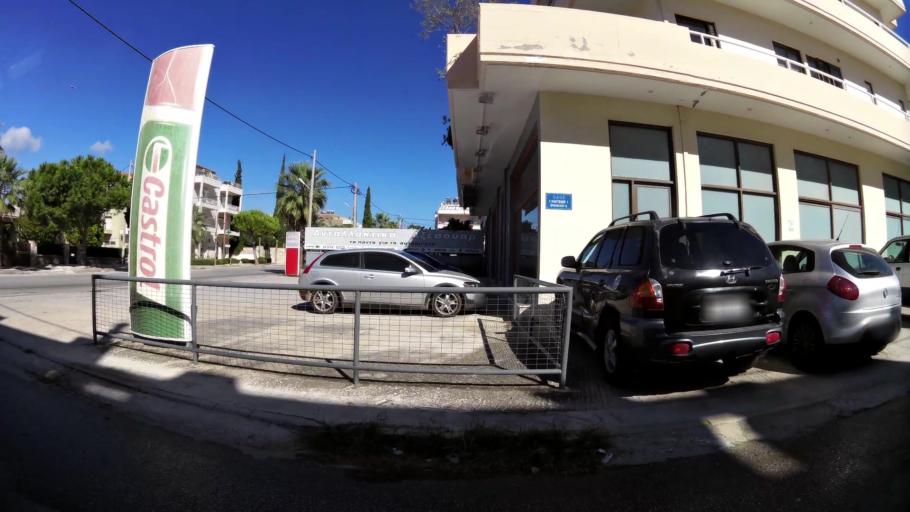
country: GR
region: Attica
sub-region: Nomarchia Anatolikis Attikis
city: Markopoulo
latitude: 37.8749
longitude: 23.9322
